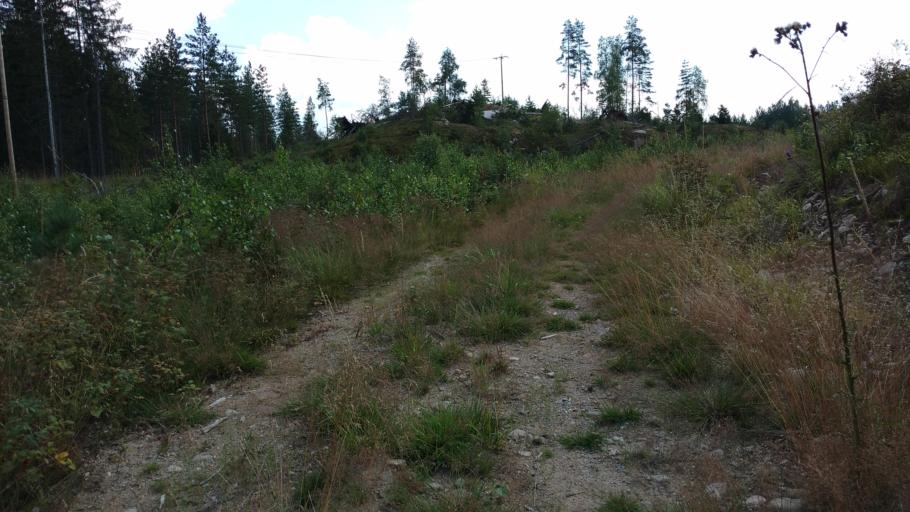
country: FI
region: Varsinais-Suomi
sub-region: Salo
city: Pertteli
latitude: 60.3945
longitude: 23.2318
